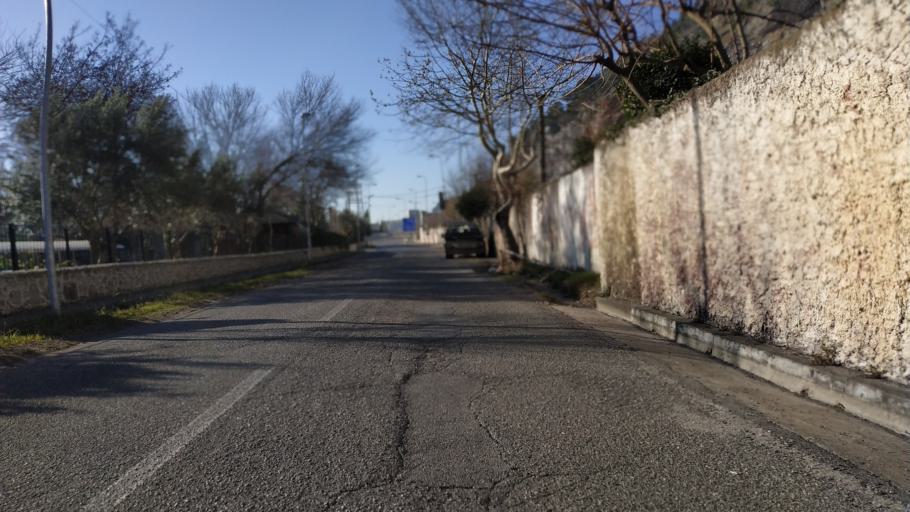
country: AL
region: Shkoder
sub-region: Rrethi i Shkodres
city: Shkoder
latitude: 42.0480
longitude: 19.4870
